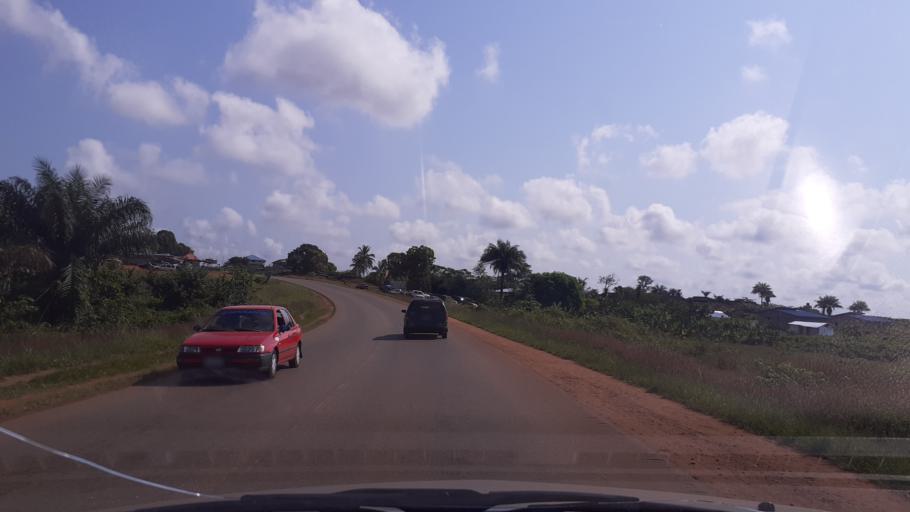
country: LR
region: Montserrado
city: Bensonville City
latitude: 6.2229
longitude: -10.5377
